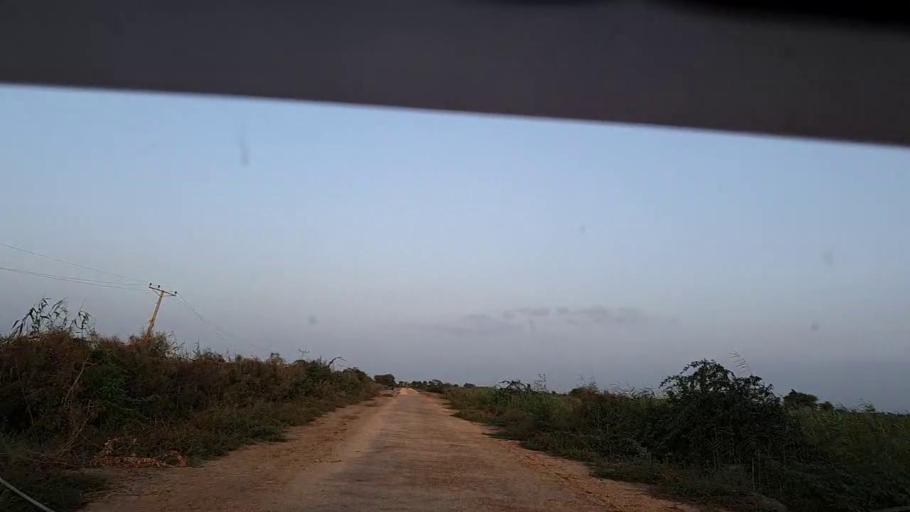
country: PK
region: Sindh
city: Kadhan
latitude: 24.5293
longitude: 68.9499
